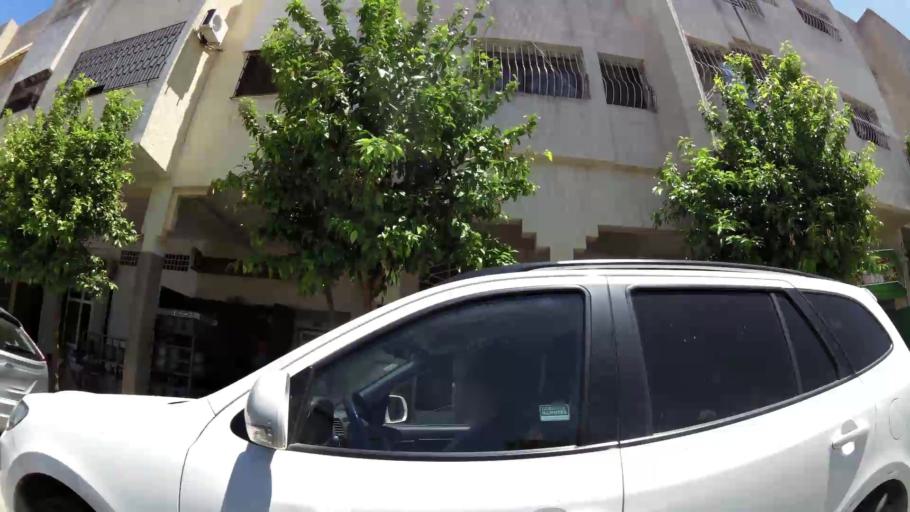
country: MA
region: Fes-Boulemane
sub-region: Fes
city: Fes
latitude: 34.0240
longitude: -5.0130
